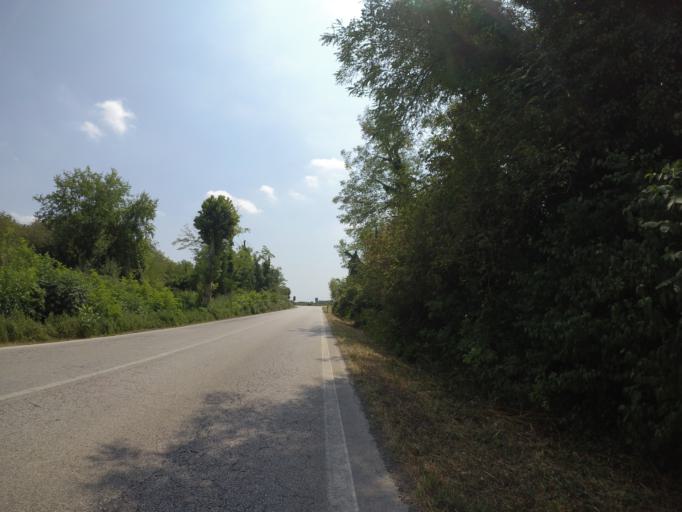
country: IT
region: Friuli Venezia Giulia
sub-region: Provincia di Udine
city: Basiliano-Vissandone
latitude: 46.0026
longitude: 13.1174
